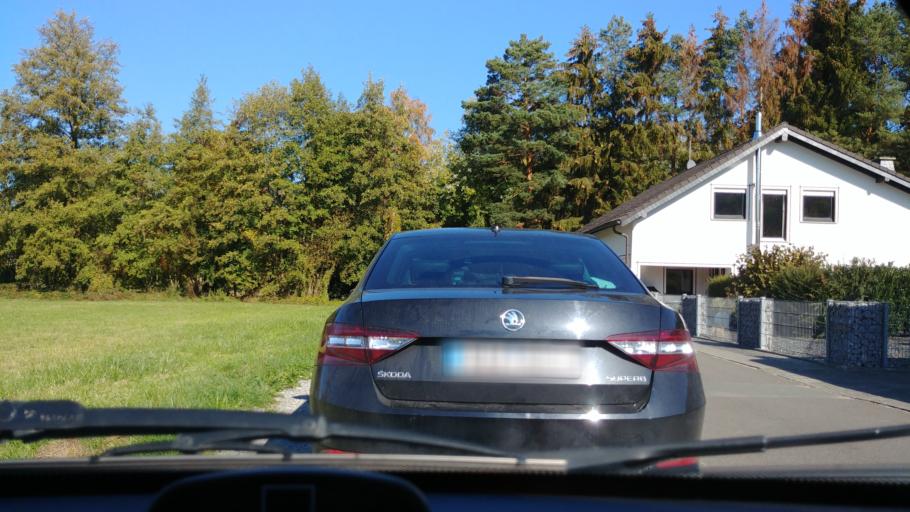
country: DE
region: Rheinland-Pfalz
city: Schiesheim
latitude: 50.2781
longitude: 8.0629
